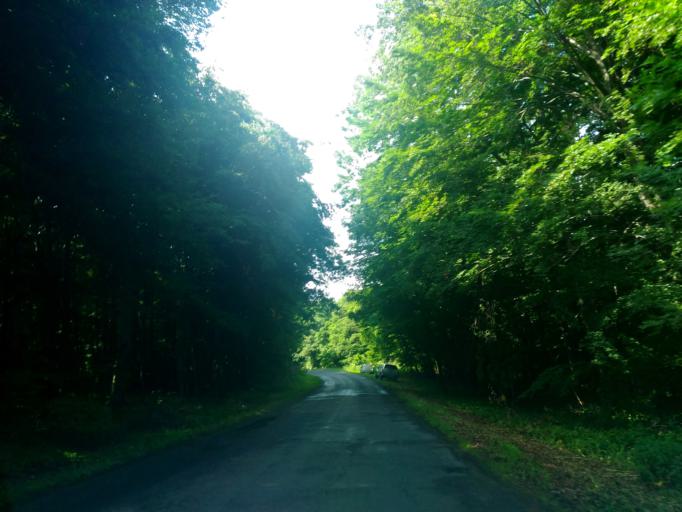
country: HU
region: Baranya
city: Pecs
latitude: 46.1303
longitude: 18.2292
